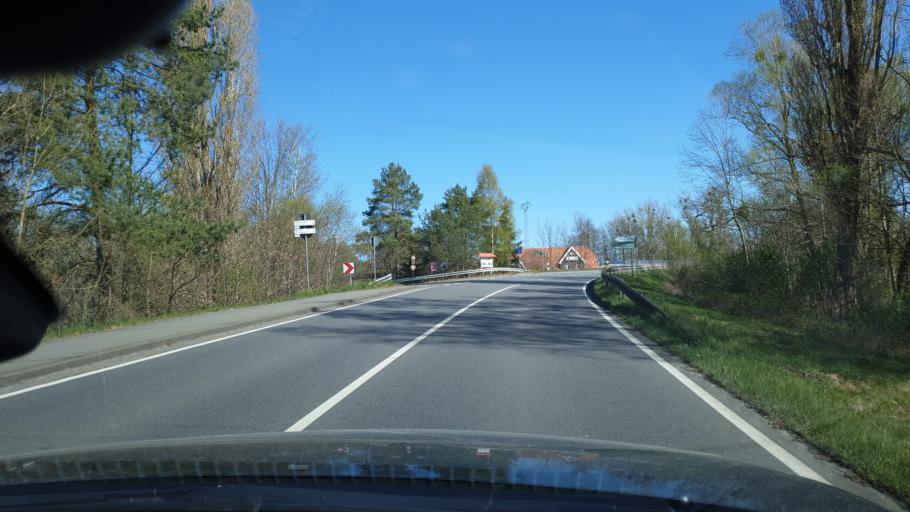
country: DE
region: Mecklenburg-Vorpommern
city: Seehof
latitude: 53.6769
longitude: 11.4495
